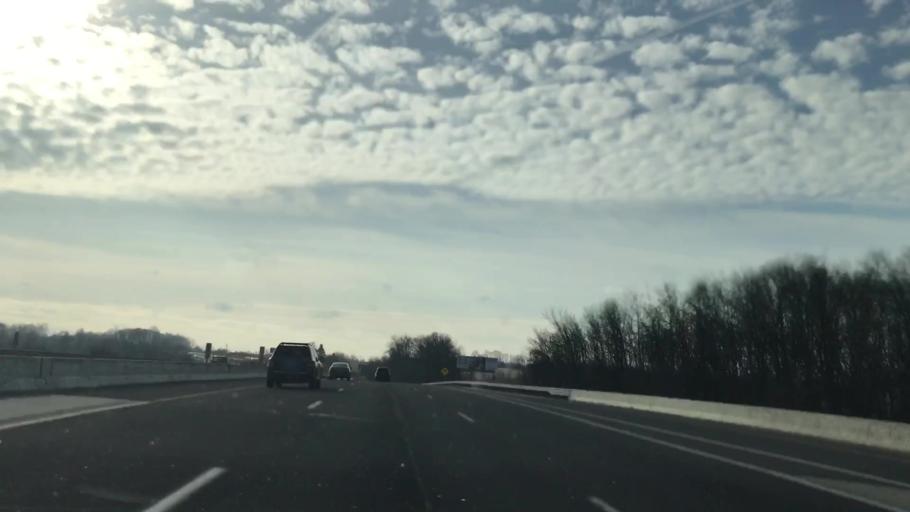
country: US
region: Wisconsin
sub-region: Washington County
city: Richfield
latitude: 43.2484
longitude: -88.1825
